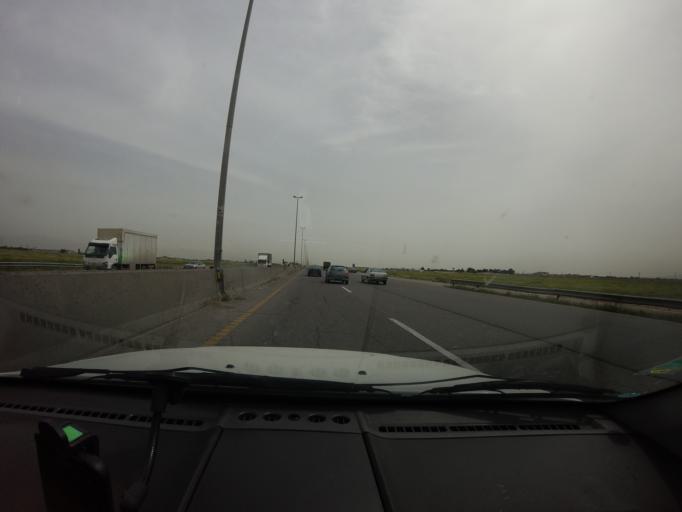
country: IR
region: Tehran
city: Robat Karim
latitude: 35.5345
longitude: 51.1001
